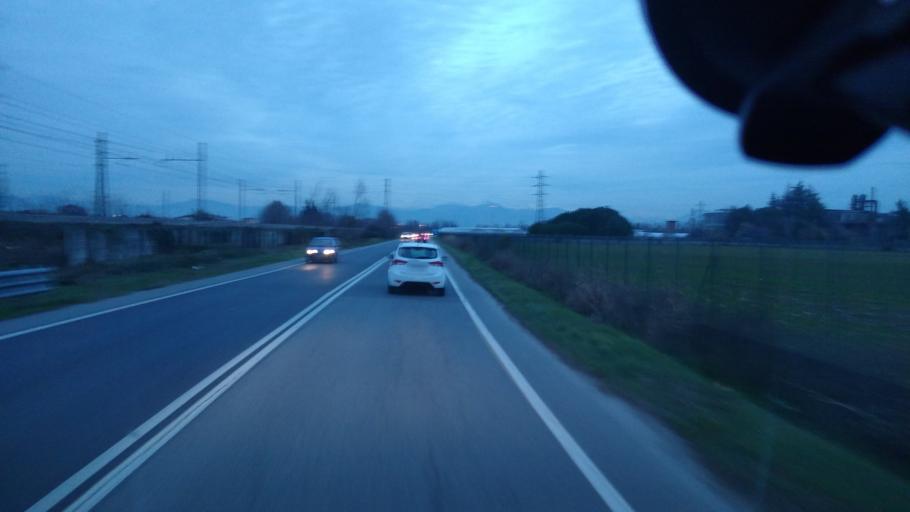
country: IT
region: Lombardy
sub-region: Provincia di Bergamo
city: Arcene
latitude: 45.5782
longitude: 9.6072
